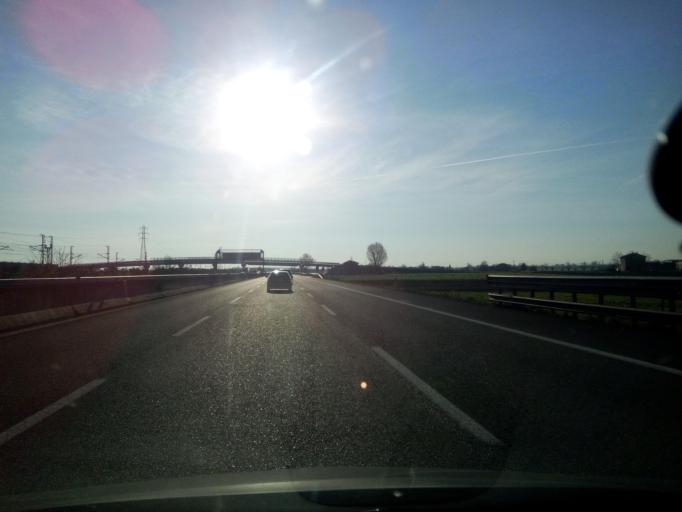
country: IT
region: Emilia-Romagna
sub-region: Provincia di Parma
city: Soragna
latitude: 44.8851
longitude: 10.1162
